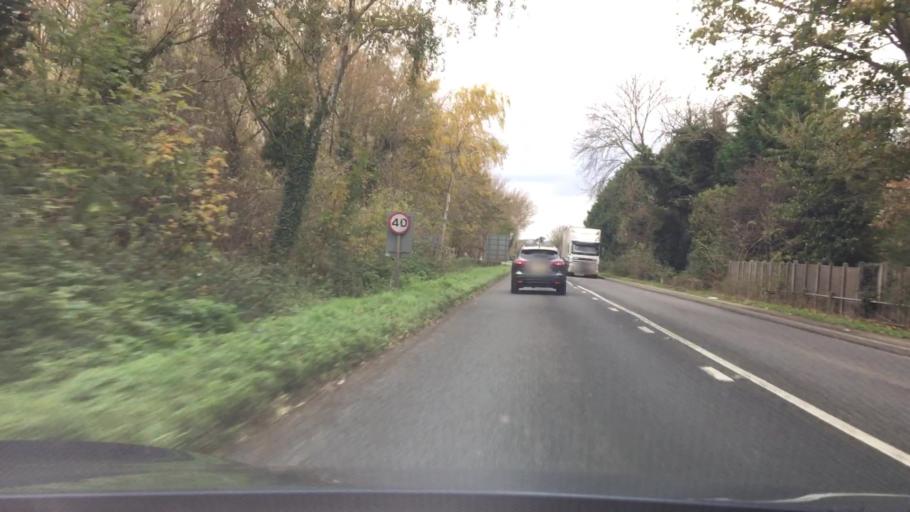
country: GB
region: England
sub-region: Nottinghamshire
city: East Bridgford
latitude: 52.9883
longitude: -0.9878
